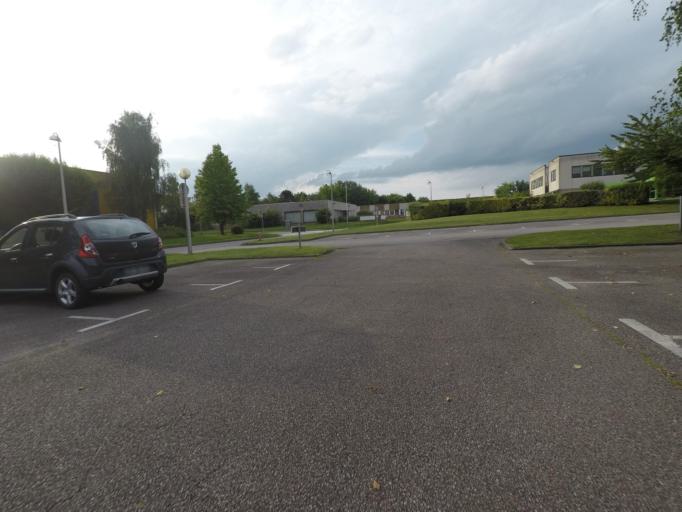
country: FR
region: Haute-Normandie
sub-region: Departement de la Seine-Maritime
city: Mont-Saint-Aignan
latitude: 49.4733
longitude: 1.0966
